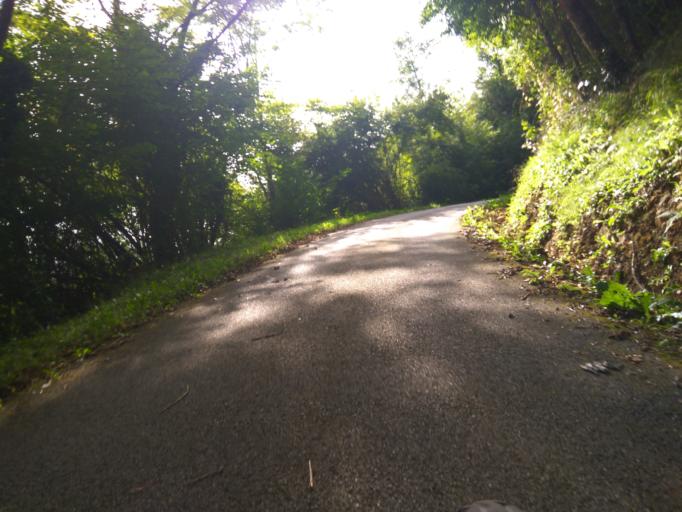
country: FR
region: Aquitaine
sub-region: Departement des Pyrenees-Atlantiques
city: Mazeres-Lezons
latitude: 43.2666
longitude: -0.3459
